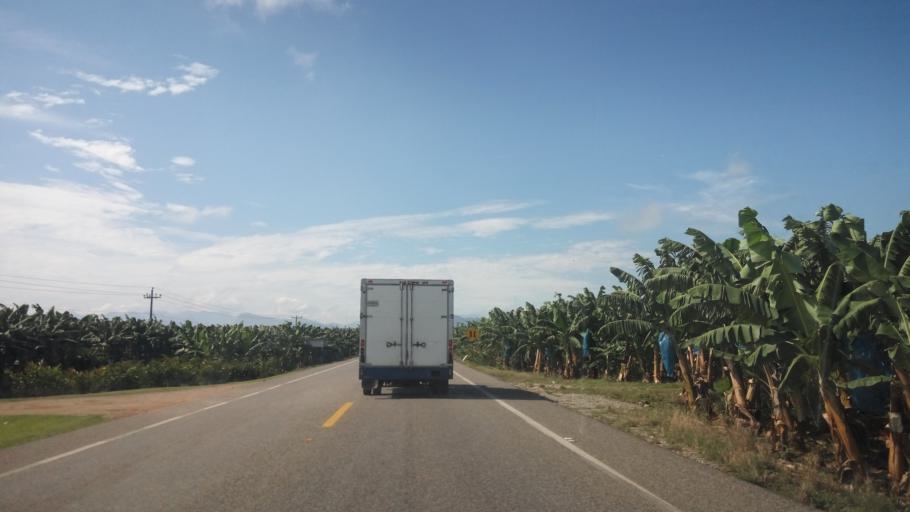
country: MX
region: Tabasco
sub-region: Teapa
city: Eureka y Belen
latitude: 17.6475
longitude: -92.9650
